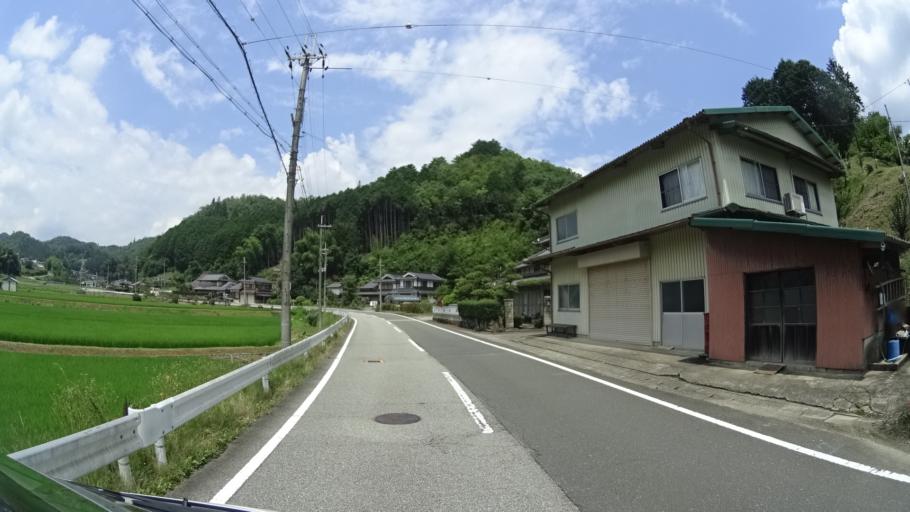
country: JP
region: Hyogo
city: Sasayama
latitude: 35.1694
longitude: 135.2570
